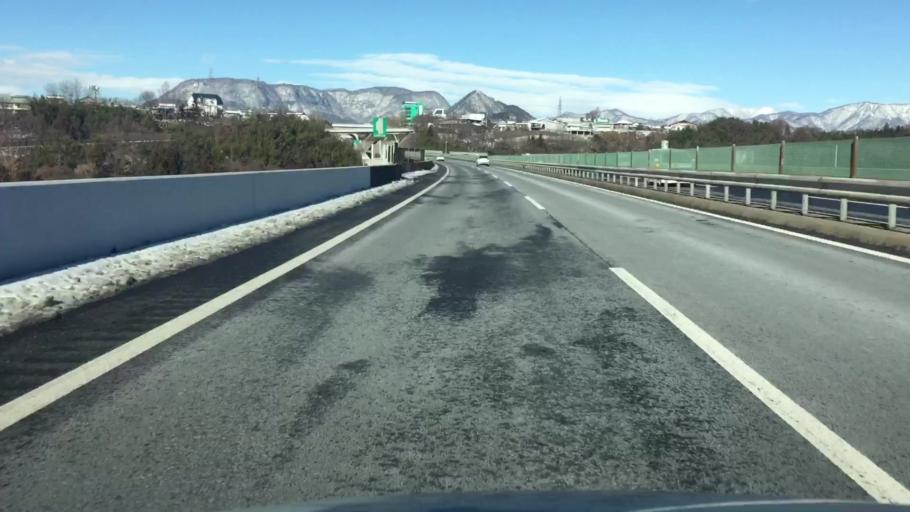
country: JP
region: Gunma
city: Numata
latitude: 36.6487
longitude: 139.0776
